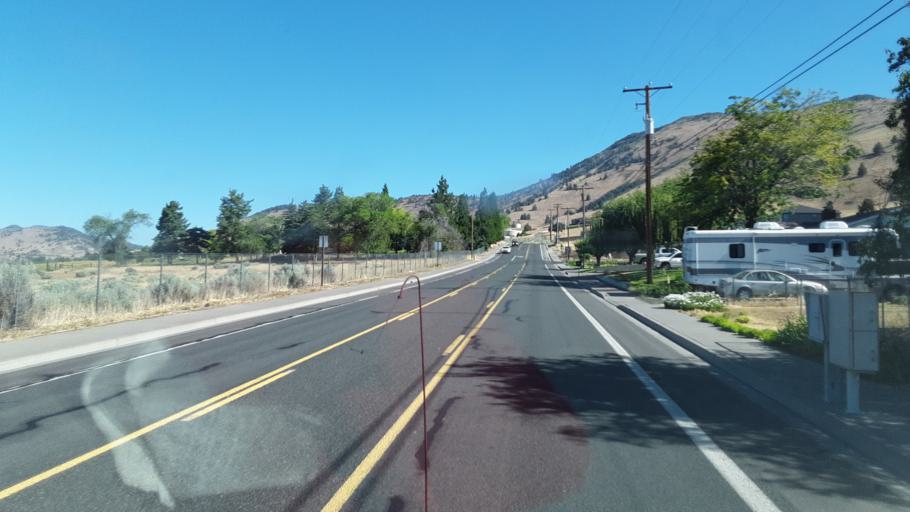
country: US
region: Oregon
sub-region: Klamath County
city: Altamont
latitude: 42.2187
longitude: -121.7129
